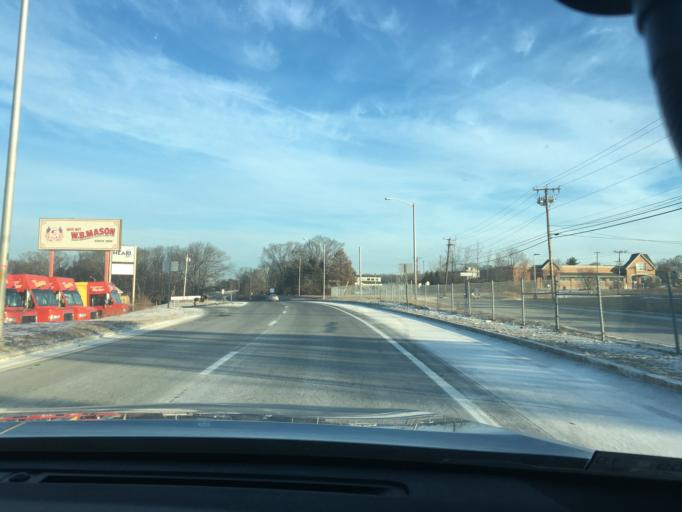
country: US
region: Rhode Island
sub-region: Kent County
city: West Warwick
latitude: 41.7329
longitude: -71.4796
